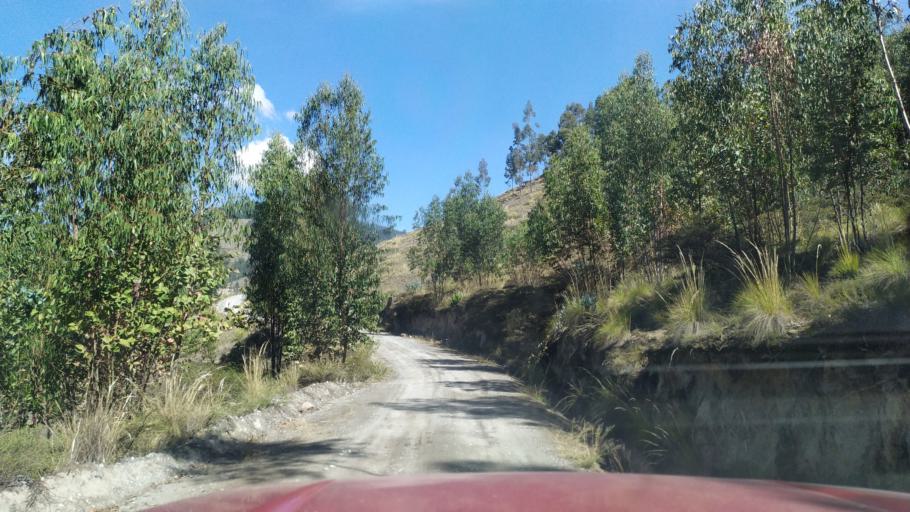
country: EC
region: Chimborazo
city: Riobamba
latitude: -1.6757
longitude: -78.6958
